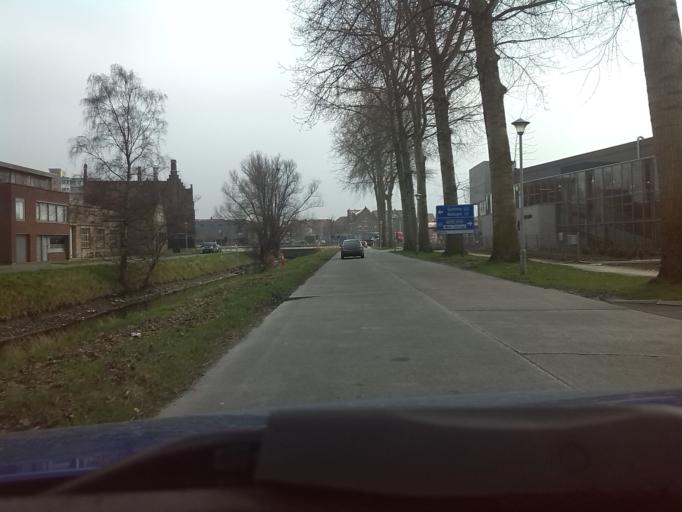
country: BE
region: Flanders
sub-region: Provincie West-Vlaanderen
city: Brugge
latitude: 51.2219
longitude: 3.2154
